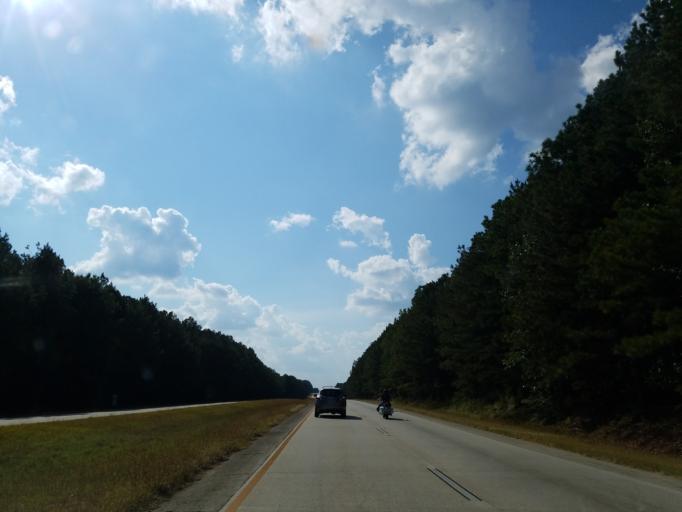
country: US
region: Georgia
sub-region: Barrow County
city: Russell
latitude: 33.9516
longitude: -83.6805
